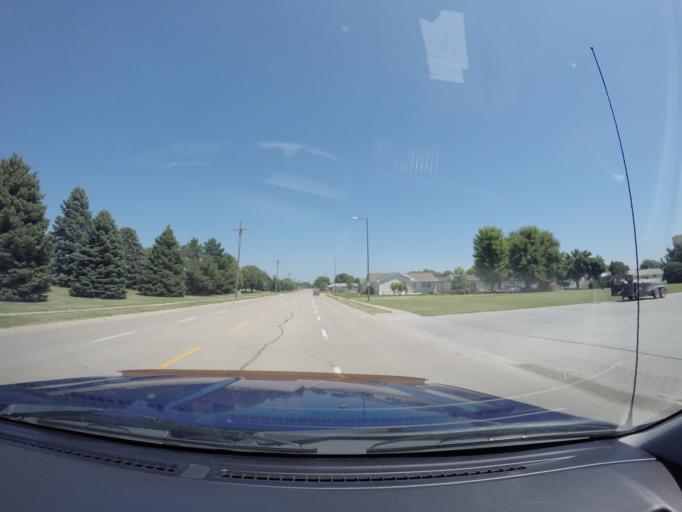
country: US
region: Nebraska
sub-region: Phelps County
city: Holdrege
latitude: 40.4488
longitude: -99.3779
